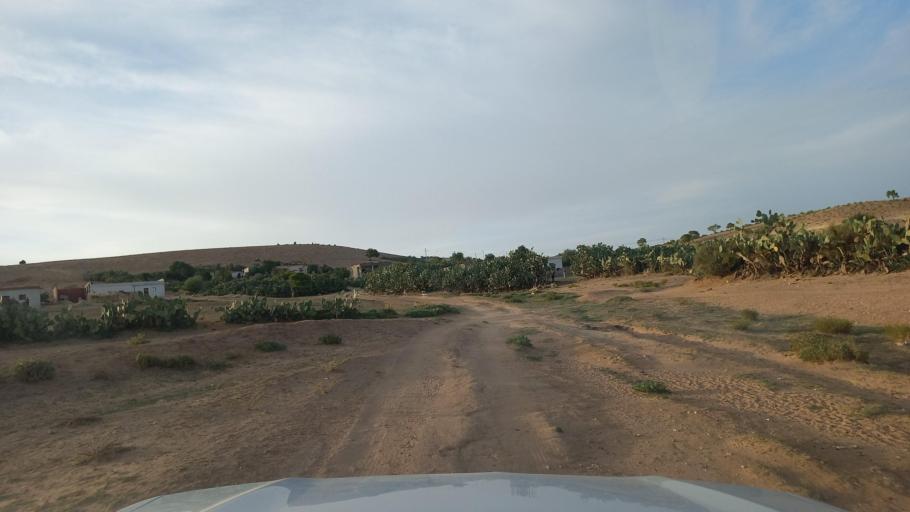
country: TN
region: Al Qasrayn
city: Sbiba
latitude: 35.4100
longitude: 8.9035
